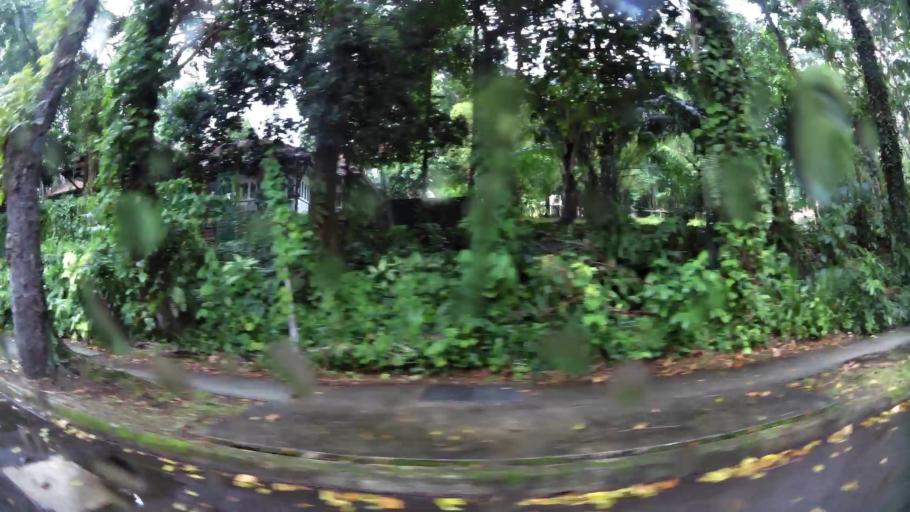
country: SG
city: Singapore
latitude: 1.3074
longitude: 103.8260
